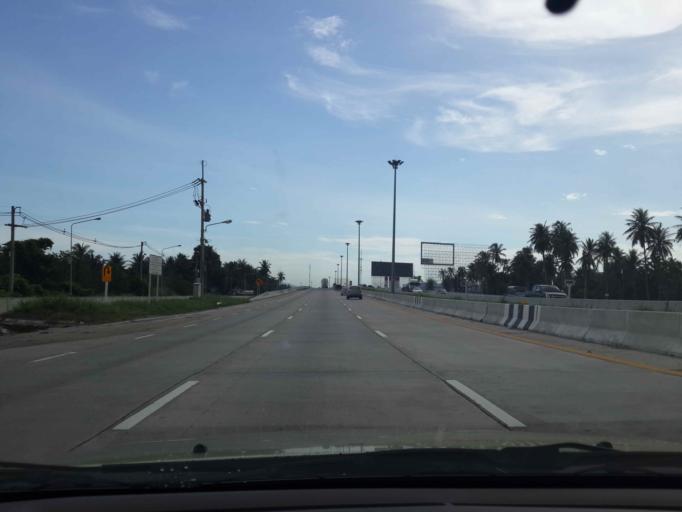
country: TH
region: Chon Buri
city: Ban Talat Bueng
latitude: 13.0042
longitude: 100.9938
